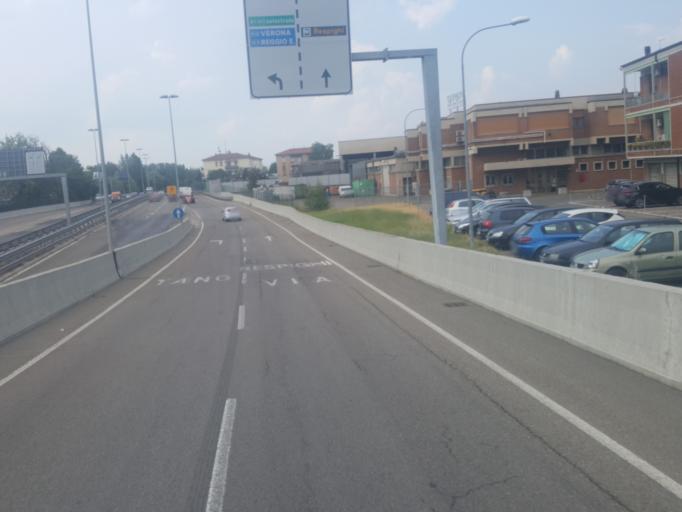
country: IT
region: Emilia-Romagna
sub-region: Provincia di Modena
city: Modena
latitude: 44.6336
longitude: 10.9577
